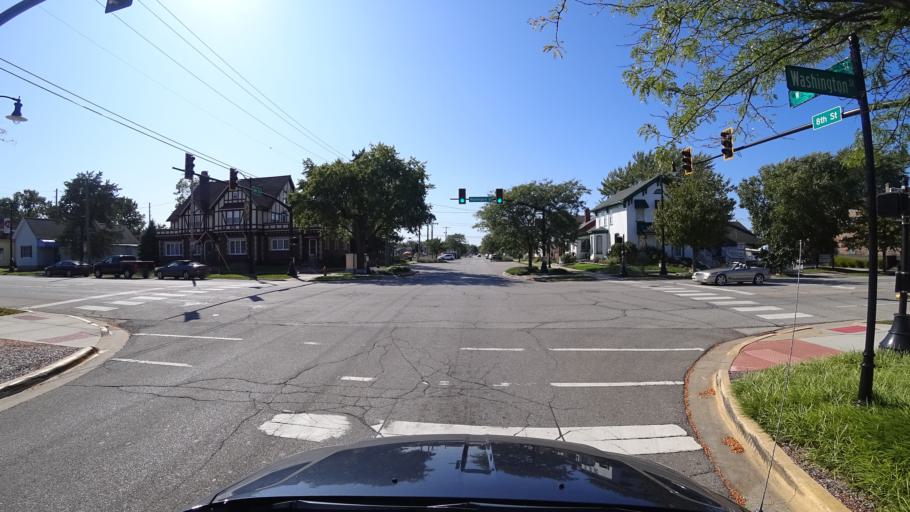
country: US
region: Indiana
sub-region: LaPorte County
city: Michigan City
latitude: 41.7136
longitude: -86.9015
